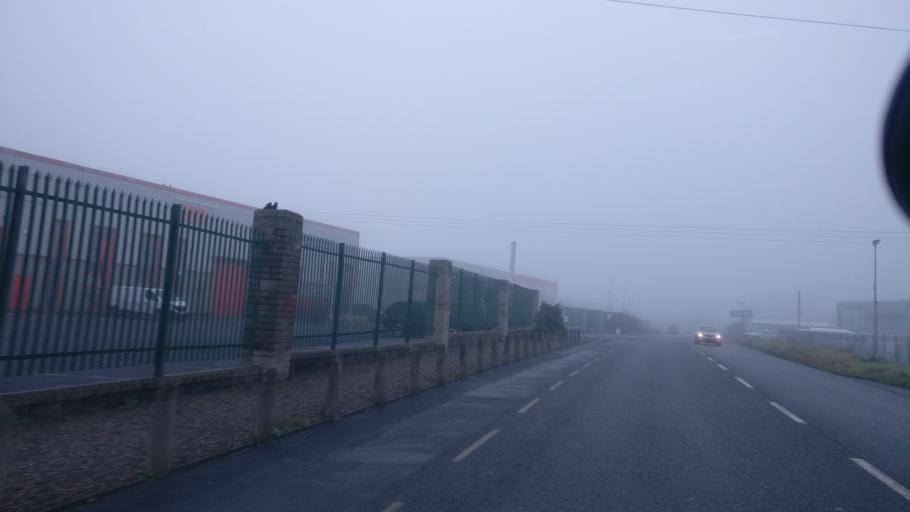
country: IE
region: Munster
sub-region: County Limerick
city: Annacotty
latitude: 52.6494
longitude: -8.5839
